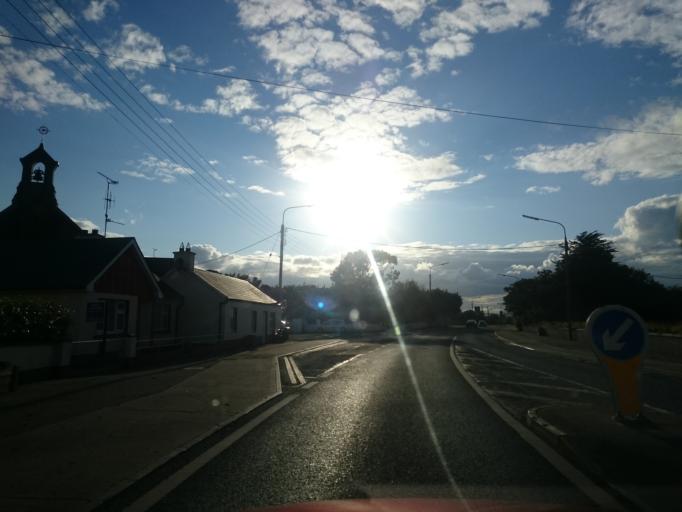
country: IE
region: Leinster
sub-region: Loch Garman
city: Ballygerry
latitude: 52.2422
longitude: -6.3565
